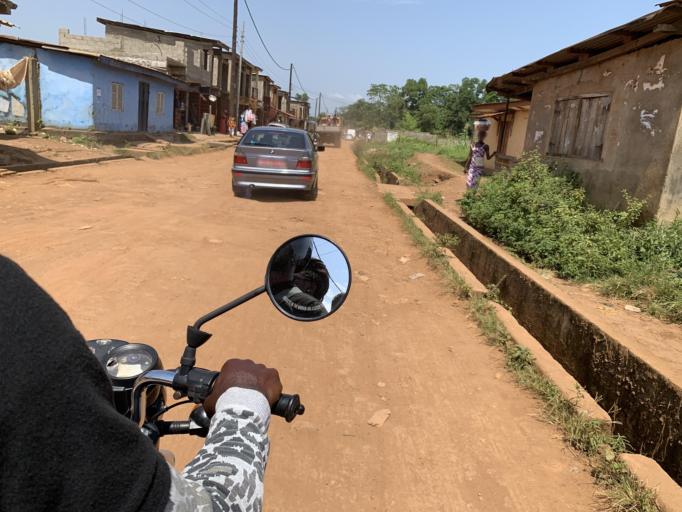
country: SL
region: Western Area
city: Hastings
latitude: 8.3816
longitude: -13.1358
